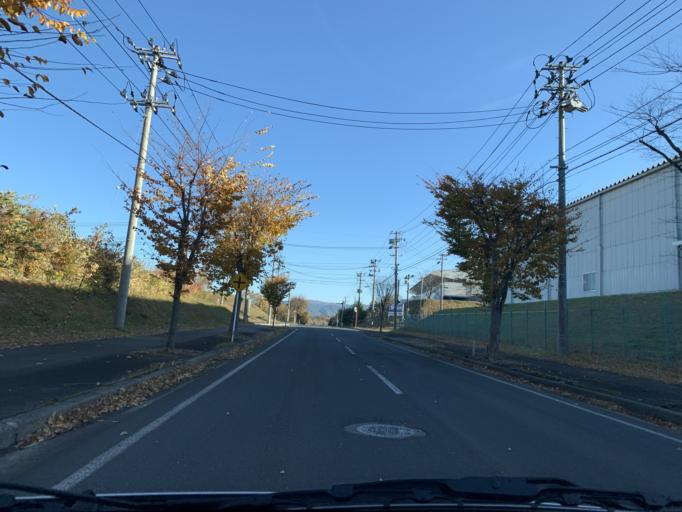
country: JP
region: Iwate
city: Mizusawa
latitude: 39.2069
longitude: 141.1818
